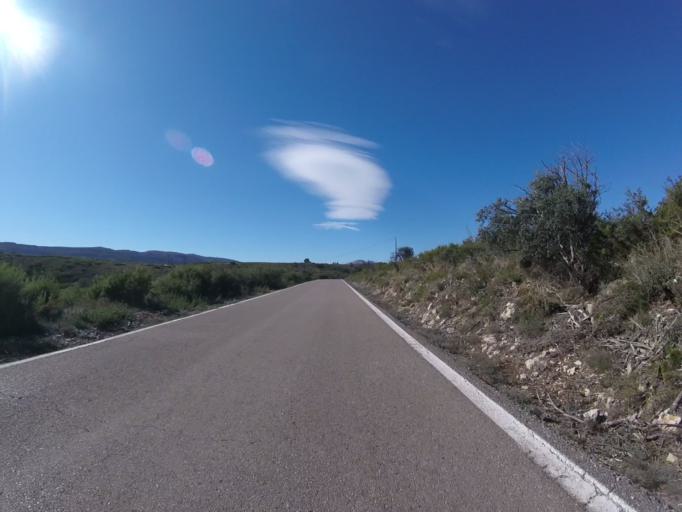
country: ES
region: Valencia
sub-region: Provincia de Castello
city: Albocasser
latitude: 40.3766
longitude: 0.0206
